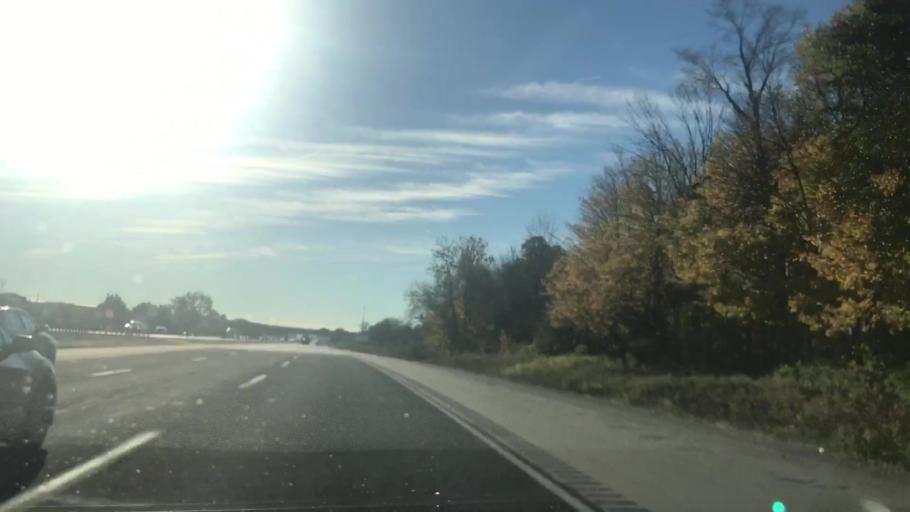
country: US
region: Wisconsin
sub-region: Washington County
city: Richfield
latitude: 43.2396
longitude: -88.1785
